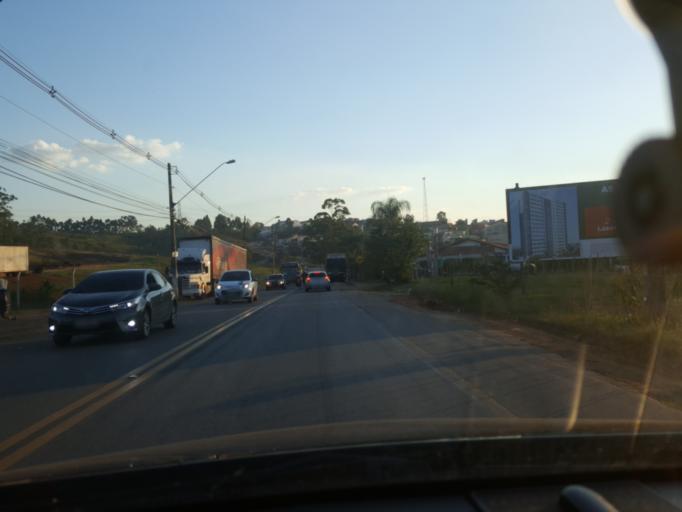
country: BR
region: Sao Paulo
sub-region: Cajamar
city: Cajamar
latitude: -23.3801
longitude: -46.8579
